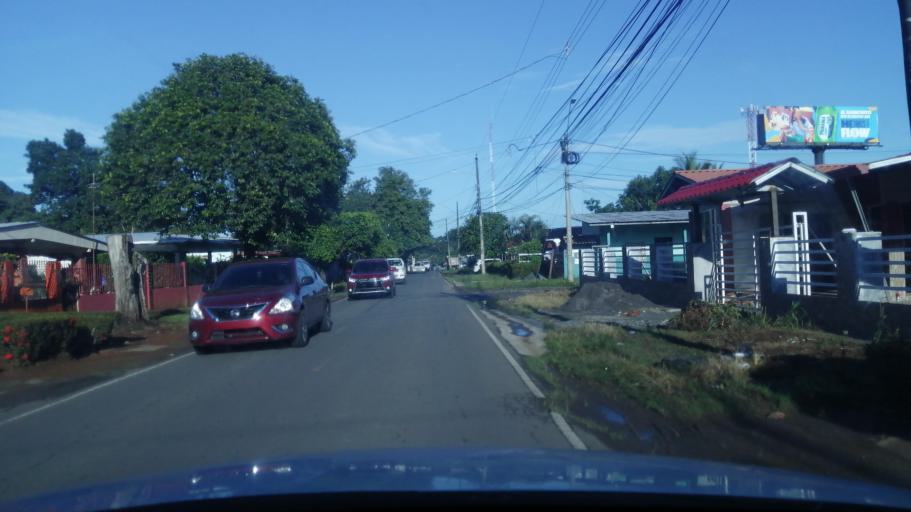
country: PA
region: Chiriqui
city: David
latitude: 8.4277
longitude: -82.4447
